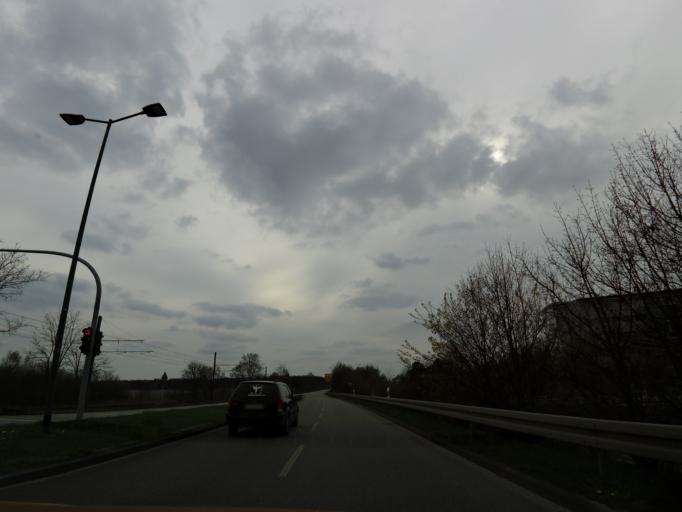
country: DE
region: Brandenburg
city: Frankfurt (Oder)
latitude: 52.3111
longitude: 14.4885
